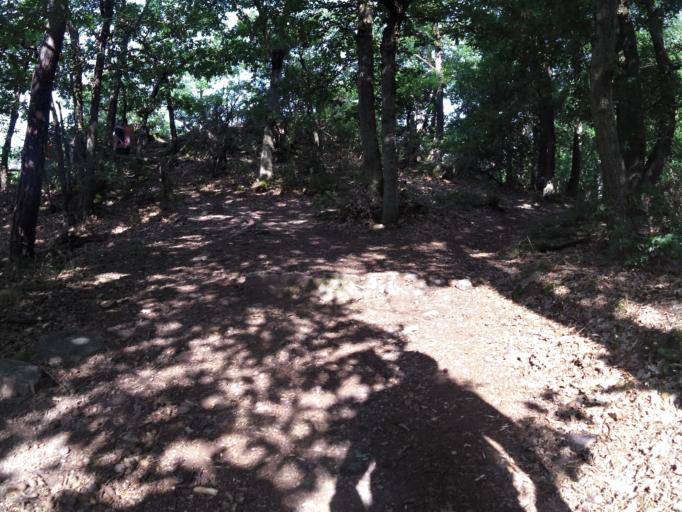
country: DE
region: Rheinland-Pfalz
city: Bad Munster am Stein-Ebernburg
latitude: 49.8171
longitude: 7.8417
